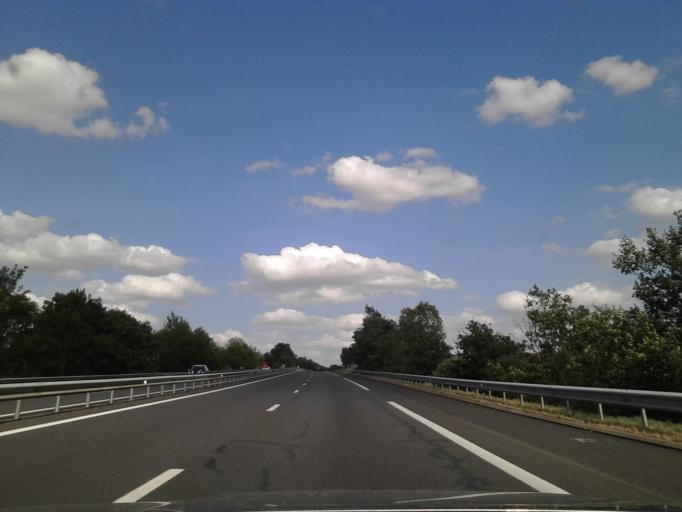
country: FR
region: Auvergne
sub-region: Departement de l'Allier
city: Montmarault
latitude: 46.3313
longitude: 2.8990
